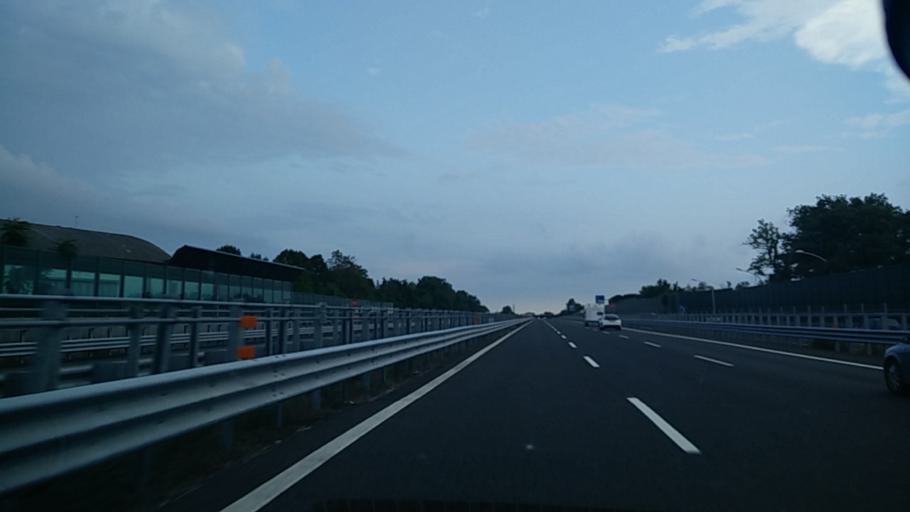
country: IT
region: Friuli Venezia Giulia
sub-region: Provincia di Udine
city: Passons
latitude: 46.0710
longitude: 13.1971
